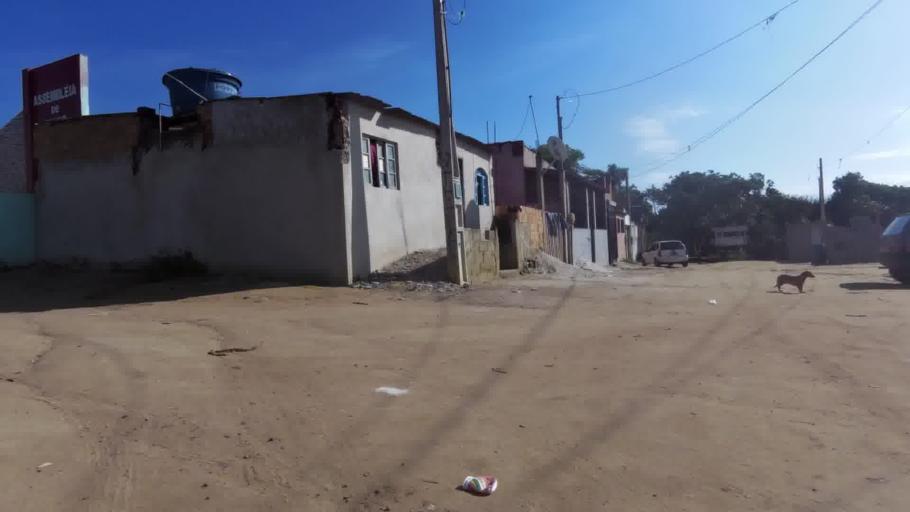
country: BR
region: Espirito Santo
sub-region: Piuma
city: Piuma
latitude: -20.8202
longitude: -40.6220
